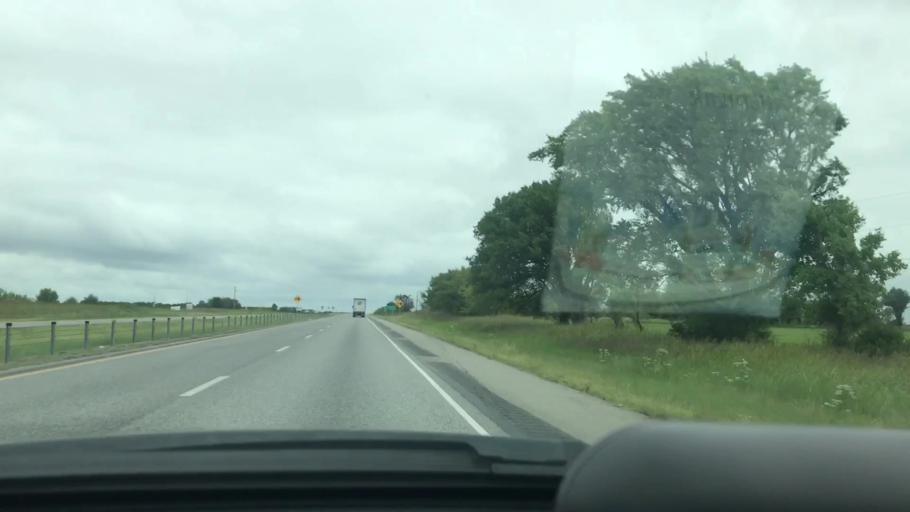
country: US
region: Oklahoma
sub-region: Pittsburg County
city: McAlester
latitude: 34.7499
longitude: -95.8944
